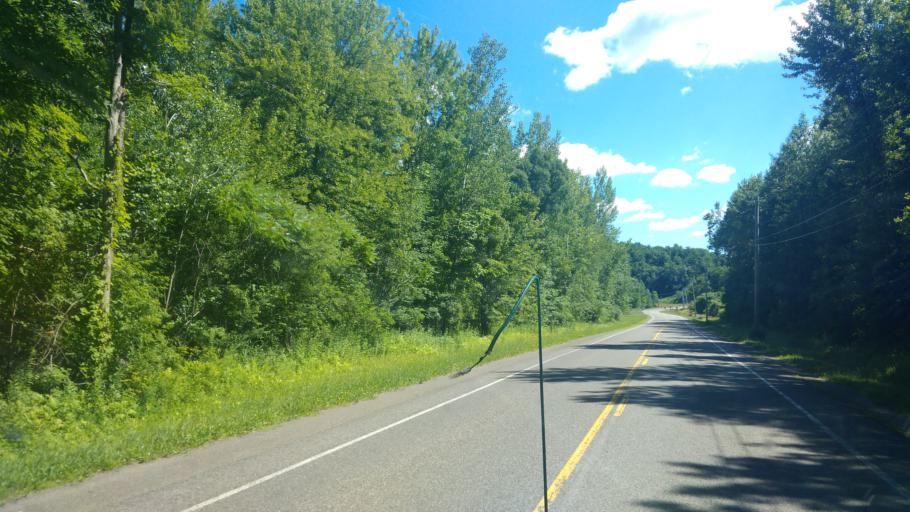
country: US
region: New York
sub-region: Wayne County
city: Sodus
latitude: 43.1800
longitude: -77.0110
